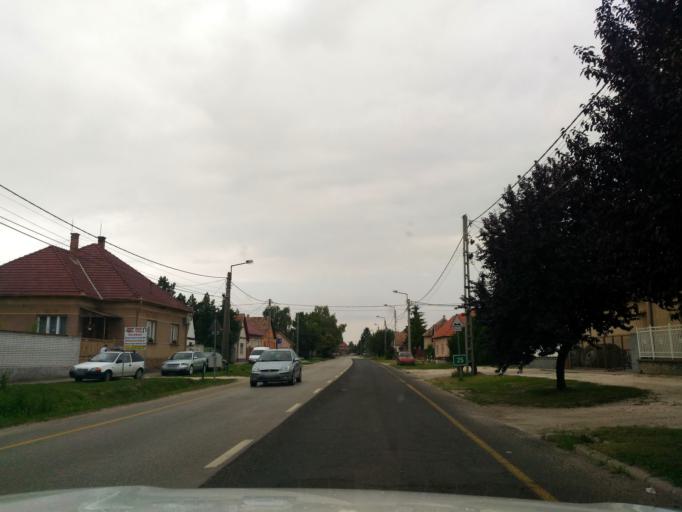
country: HU
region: Pest
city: Alsonemedi
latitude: 47.3087
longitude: 19.1745
